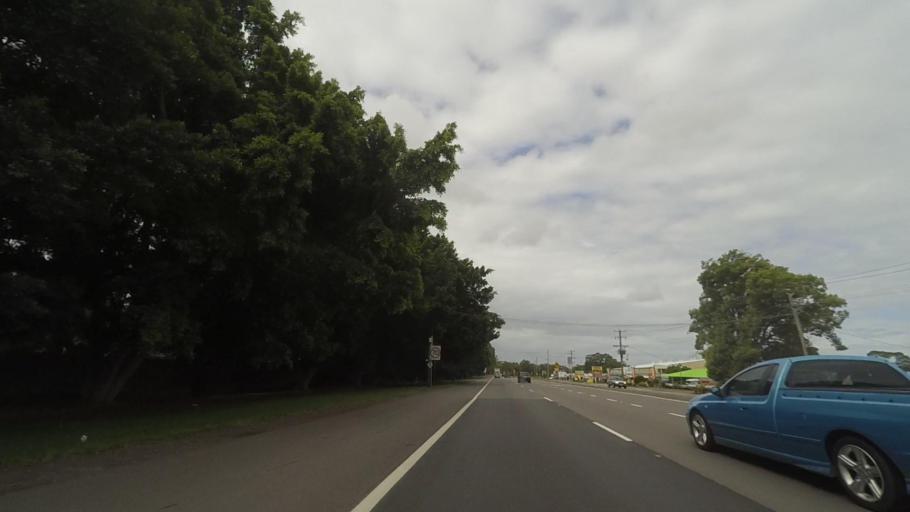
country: AU
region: New South Wales
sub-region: Port Stephens Shire
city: Raymond Terrace
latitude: -32.7851
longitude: 151.7326
